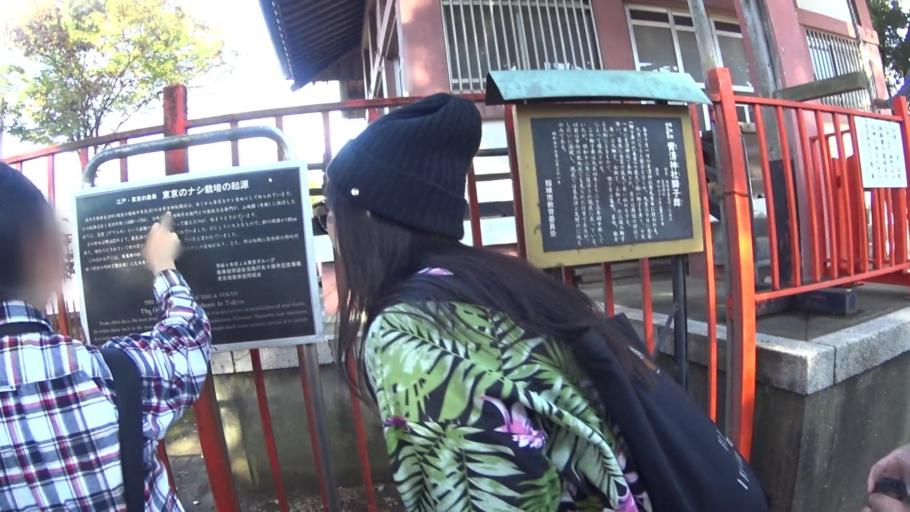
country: JP
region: Tokyo
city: Chofugaoka
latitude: 35.6426
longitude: 139.5011
